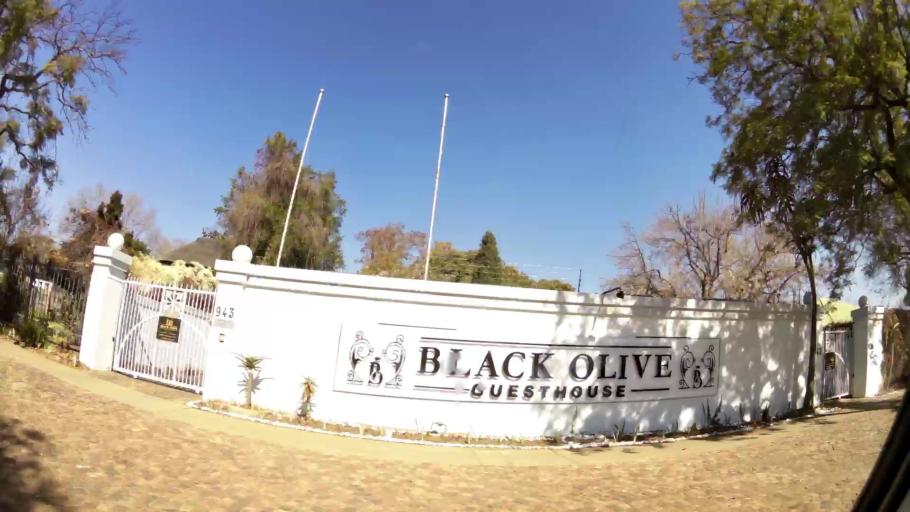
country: ZA
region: Gauteng
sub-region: City of Tshwane Metropolitan Municipality
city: Pretoria
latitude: -25.7677
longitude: 28.2389
